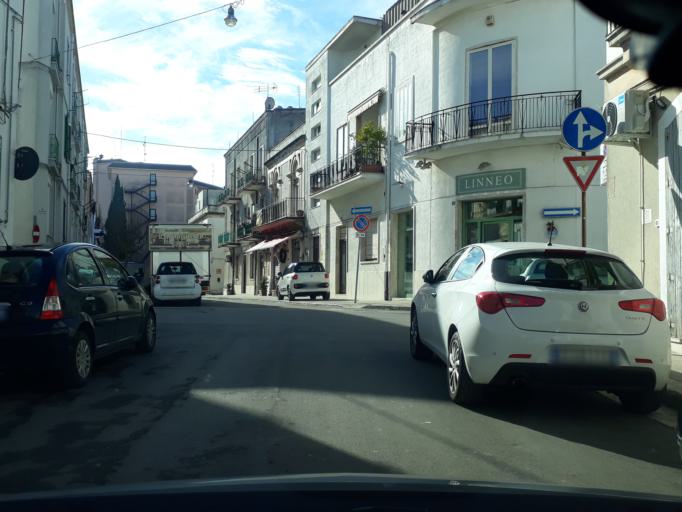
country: IT
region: Apulia
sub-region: Provincia di Taranto
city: Martina Franca
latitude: 40.7026
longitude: 17.3428
